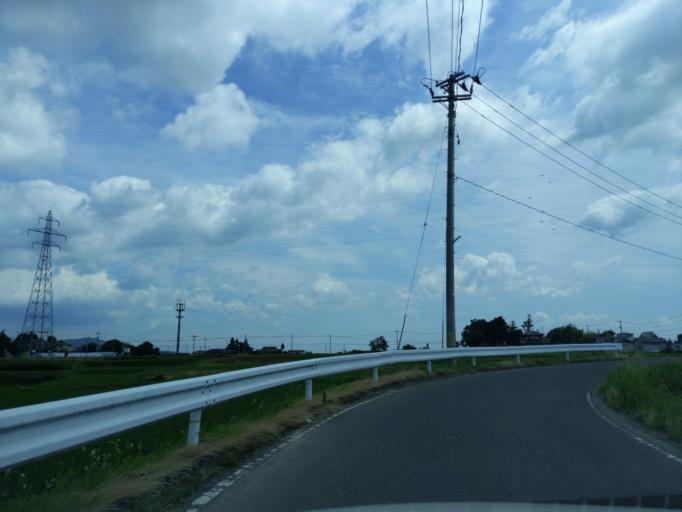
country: JP
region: Fukushima
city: Koriyama
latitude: 37.4405
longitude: 140.3552
